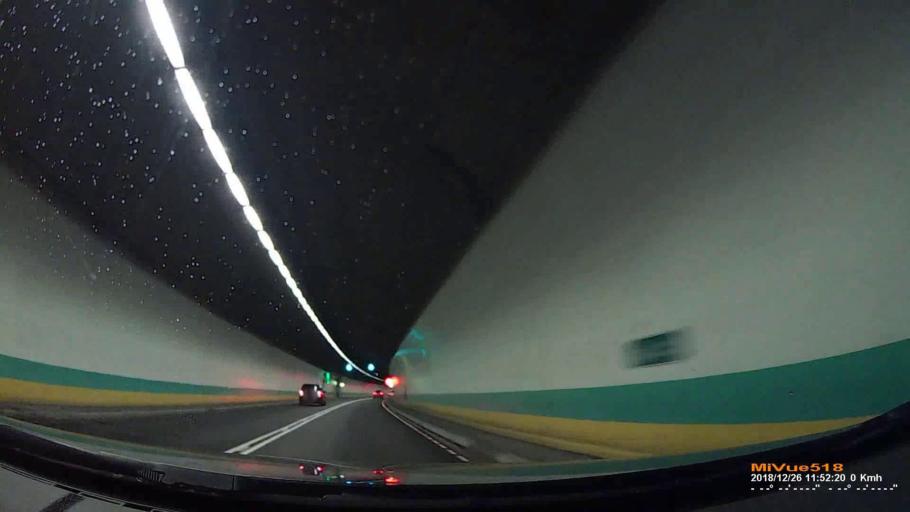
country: TW
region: Taiwan
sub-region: Keelung
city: Keelung
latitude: 24.9675
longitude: 121.6839
